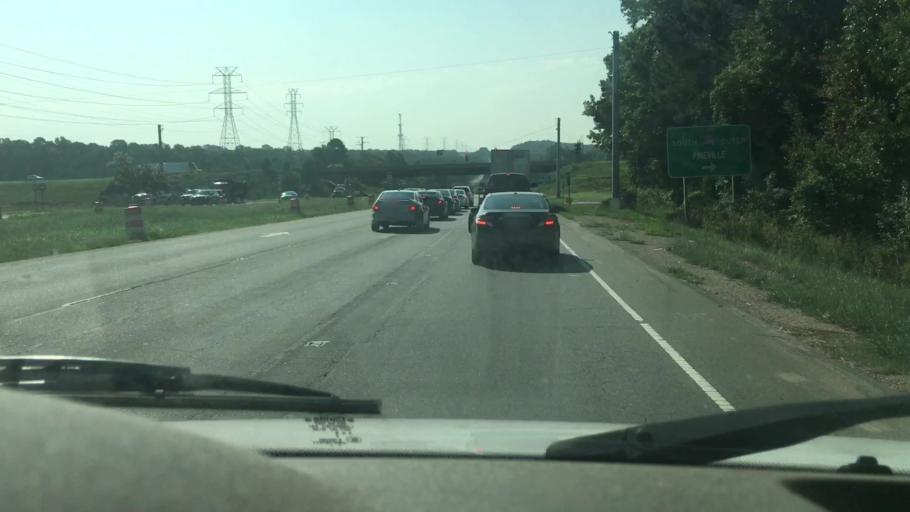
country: US
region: North Carolina
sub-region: Gaston County
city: Mount Holly
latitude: 35.3234
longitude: -80.9428
